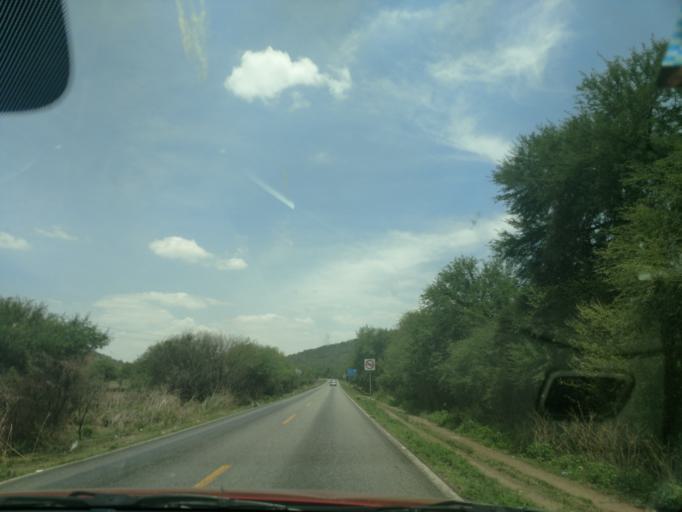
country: MX
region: San Luis Potosi
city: Ciudad Fernandez
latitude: 21.9969
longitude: -100.1390
